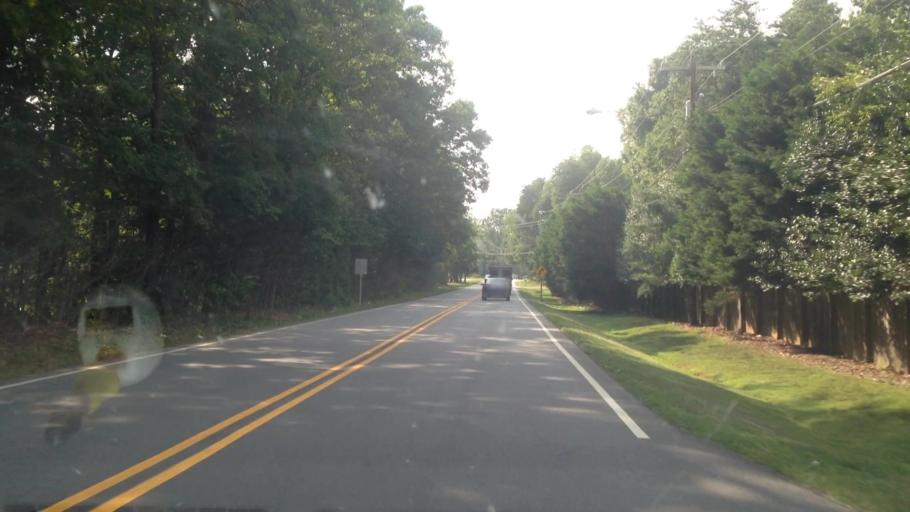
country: US
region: North Carolina
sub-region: Forsyth County
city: Kernersville
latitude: 36.1222
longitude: -80.1086
